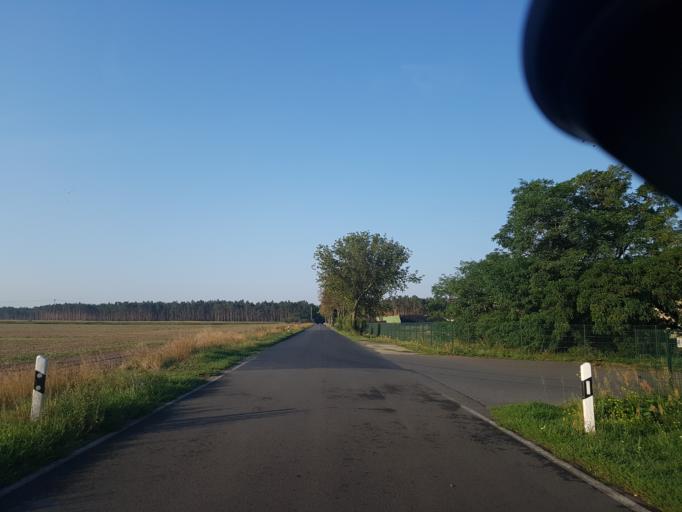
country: DE
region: Saxony-Anhalt
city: Holzdorf
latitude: 51.8109
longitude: 13.1434
